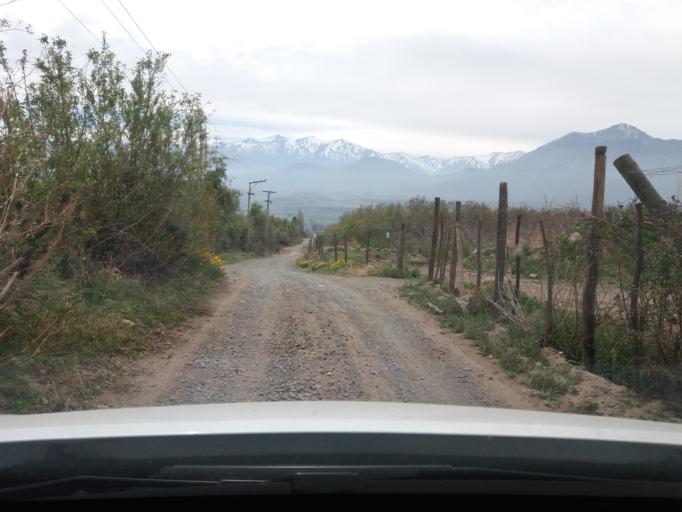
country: CL
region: Valparaiso
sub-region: Provincia de Los Andes
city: Los Andes
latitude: -32.8494
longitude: -70.5560
